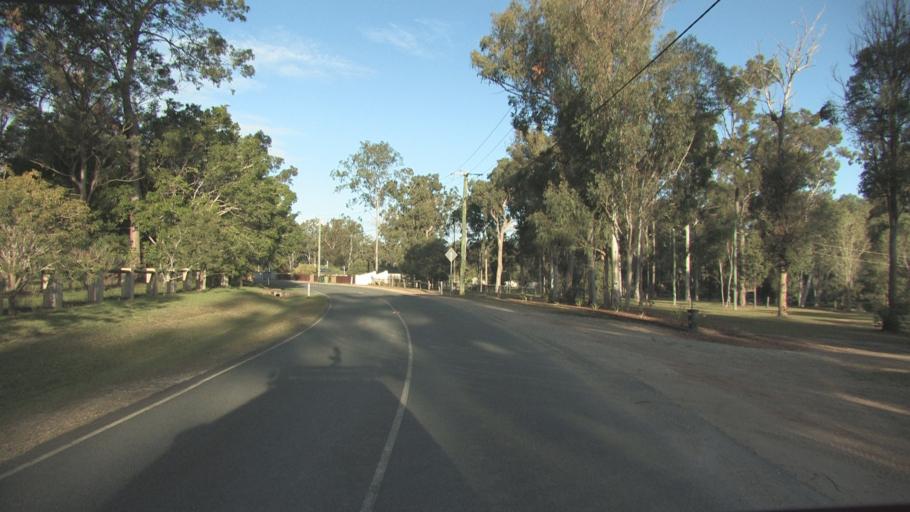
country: AU
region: Queensland
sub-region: Logan
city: Waterford West
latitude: -27.7326
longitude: 153.1378
